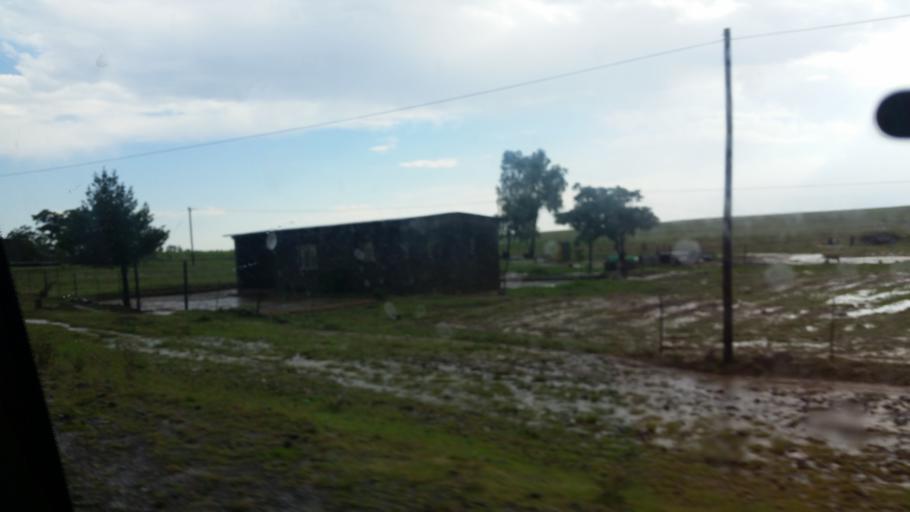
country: LS
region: Mafeteng
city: Mafeteng
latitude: -29.7610
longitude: 27.1739
